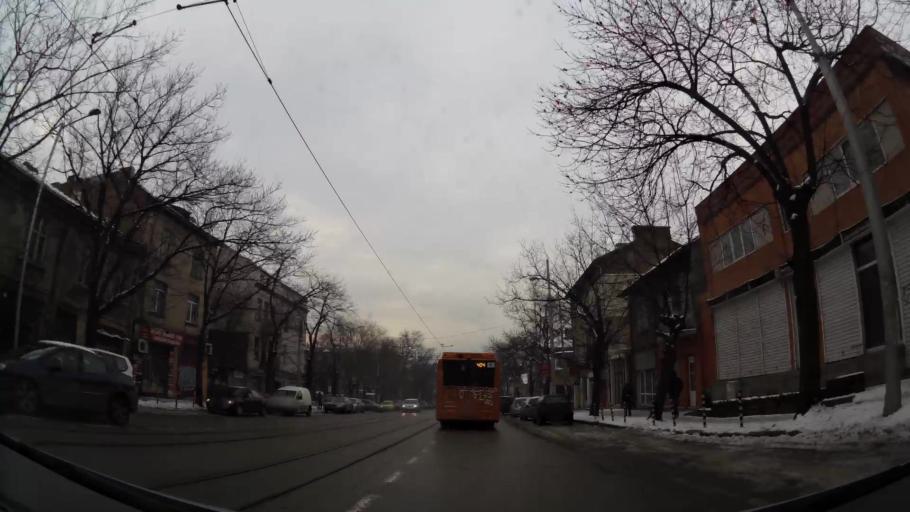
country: BG
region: Sofia-Capital
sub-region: Stolichna Obshtina
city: Sofia
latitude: 42.7071
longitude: 23.3179
